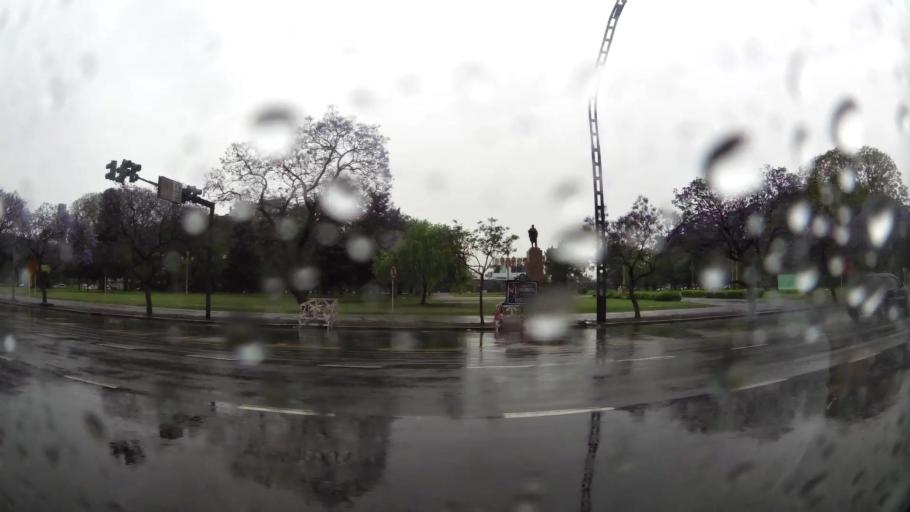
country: AR
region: Buenos Aires F.D.
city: Retiro
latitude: -34.5829
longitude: -58.3980
